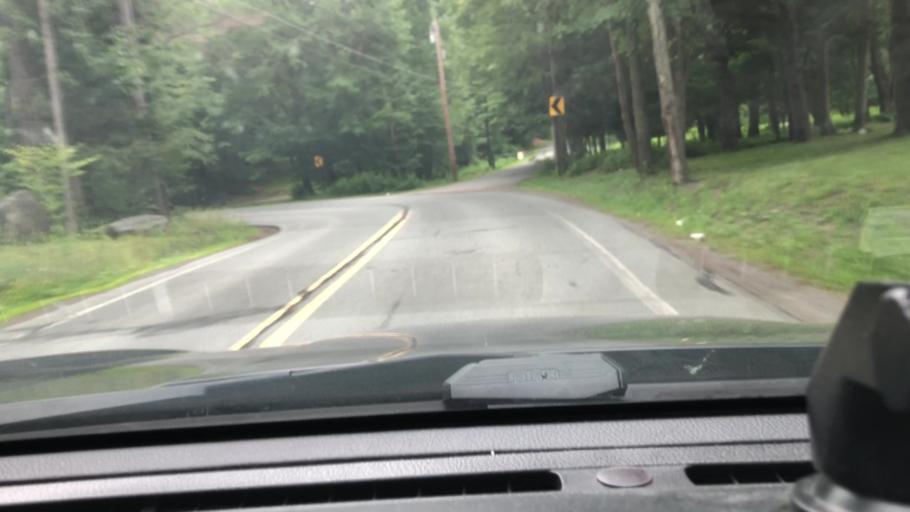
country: US
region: Pennsylvania
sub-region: Lackawanna County
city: Moscow
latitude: 41.2517
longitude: -75.4958
